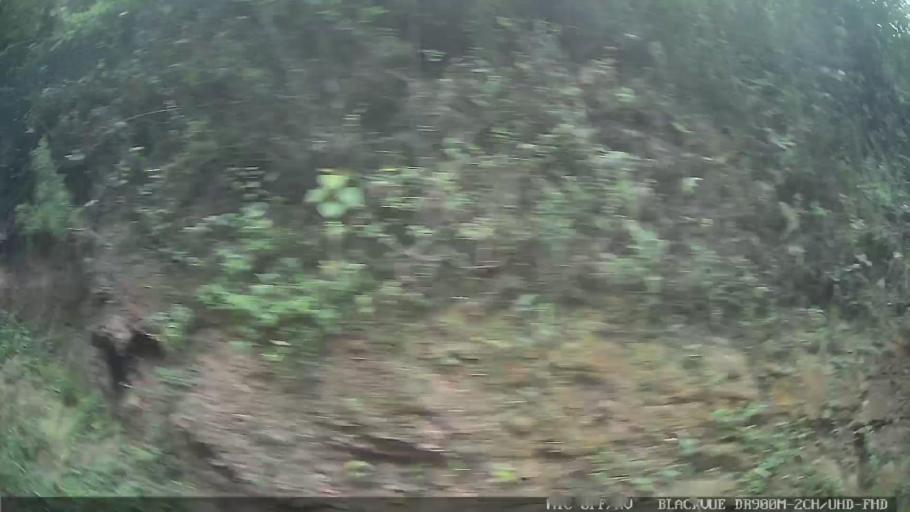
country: BR
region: Sao Paulo
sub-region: Ribeirao Pires
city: Ribeirao Pires
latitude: -23.7270
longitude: -46.4118
